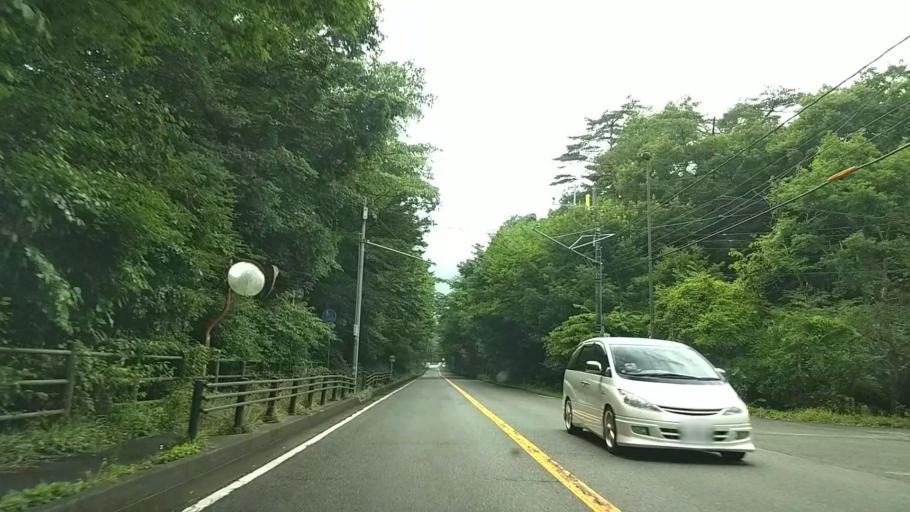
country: JP
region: Yamanashi
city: Fujikawaguchiko
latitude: 35.4672
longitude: 138.6092
